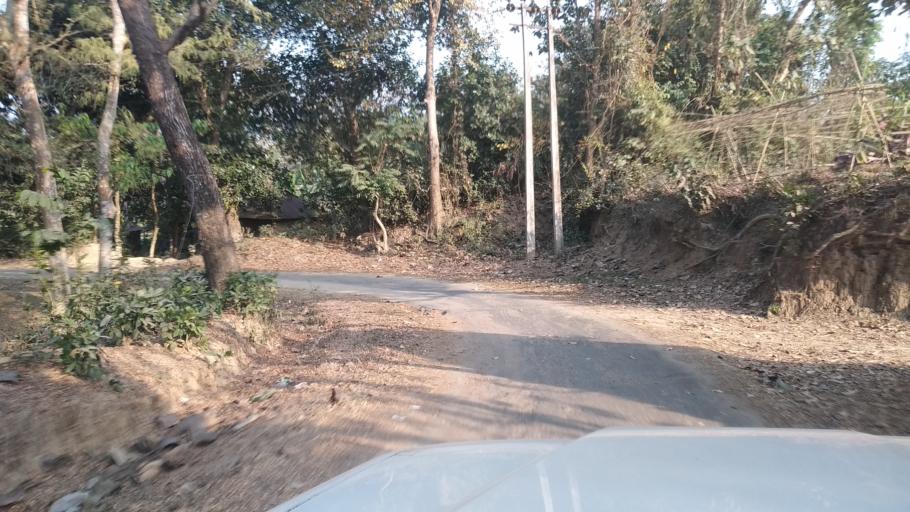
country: IN
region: Tripura
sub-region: West Tripura
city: Sonamura
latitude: 23.4282
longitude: 91.3155
